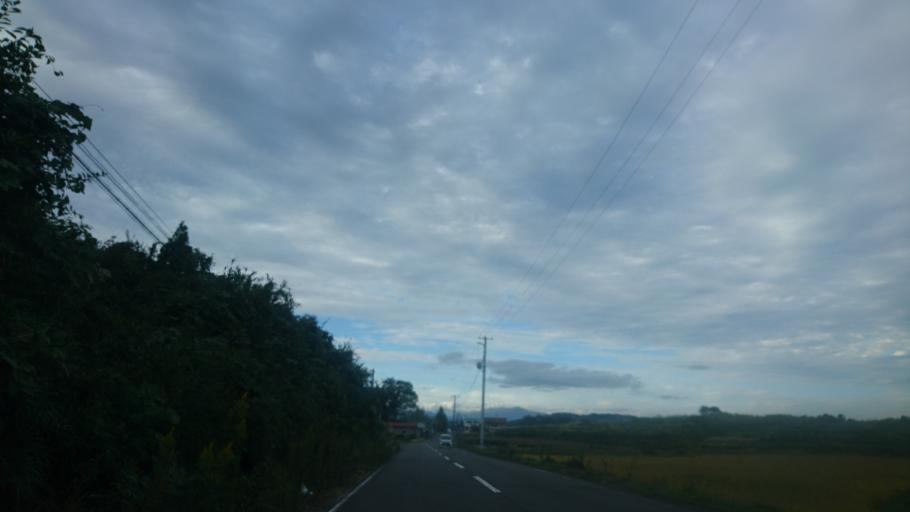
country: JP
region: Fukushima
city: Sukagawa
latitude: 37.3143
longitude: 140.2673
